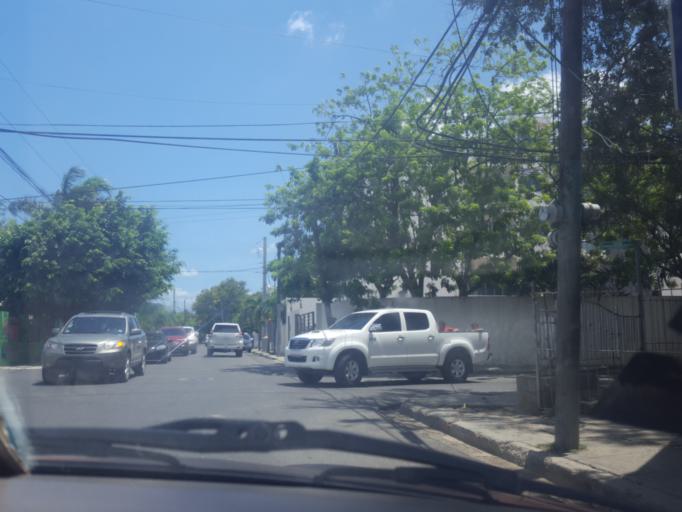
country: DO
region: Santiago
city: Santiago de los Caballeros
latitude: 19.4712
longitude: -70.6644
